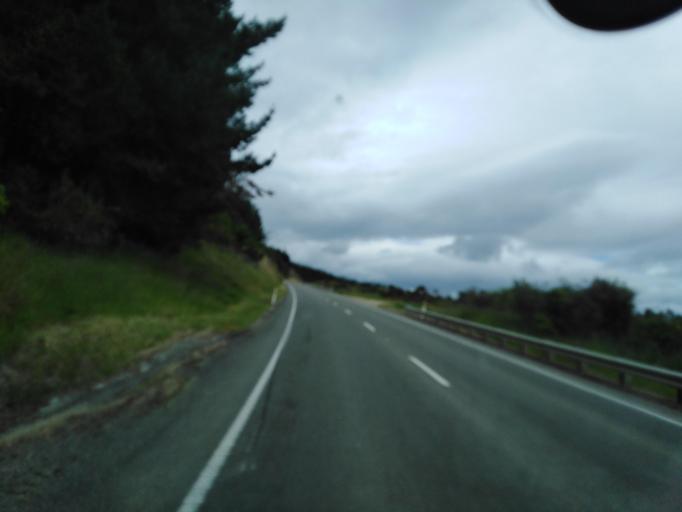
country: NZ
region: Tasman
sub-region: Tasman District
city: Wakefield
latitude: -41.4790
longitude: 172.9199
